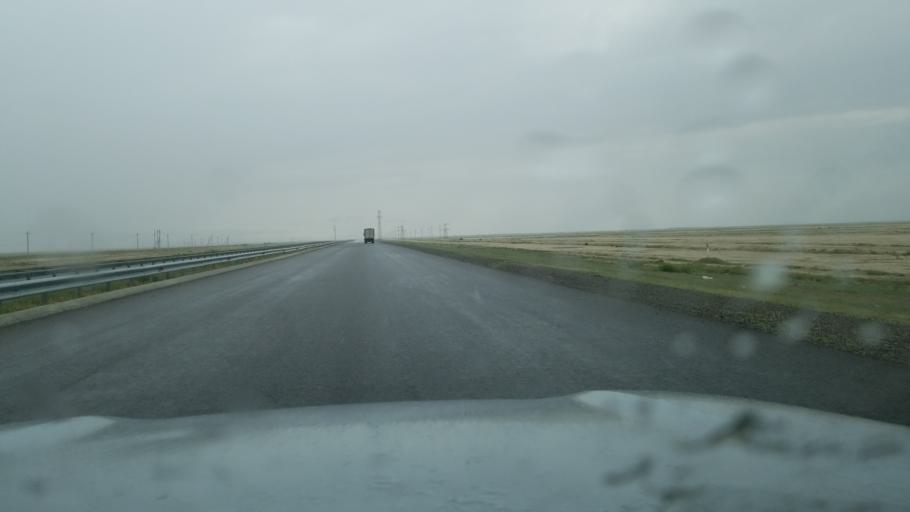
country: TM
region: Balkan
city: Serdar
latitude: 39.0185
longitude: 56.2152
